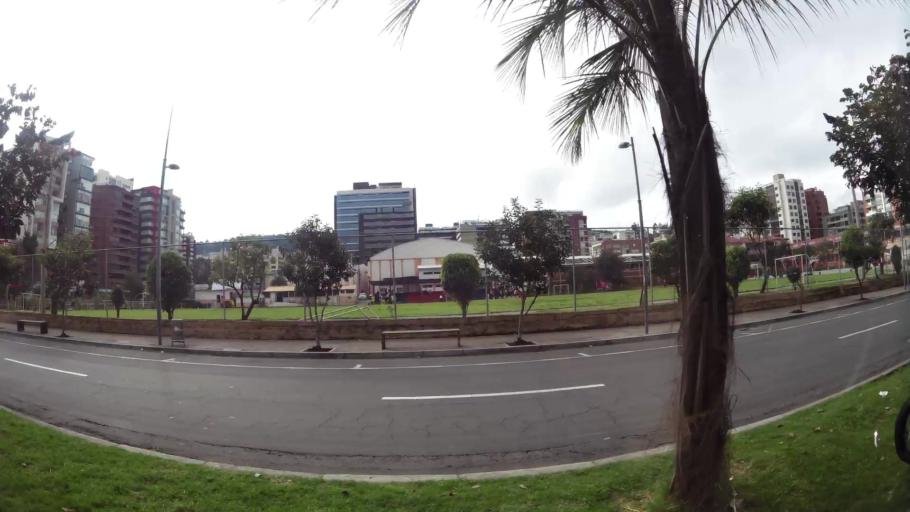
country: EC
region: Pichincha
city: Quito
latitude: -0.1825
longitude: -78.4804
